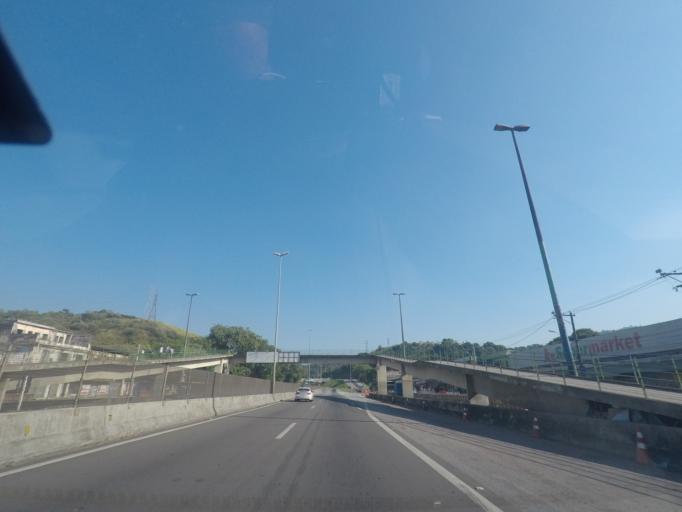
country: BR
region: Rio de Janeiro
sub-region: Duque De Caxias
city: Duque de Caxias
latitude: -22.6423
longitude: -43.2837
